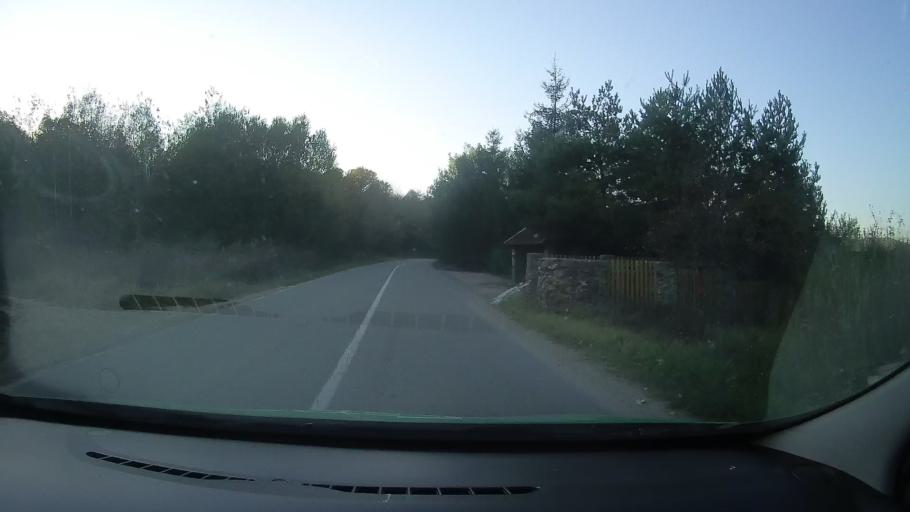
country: RO
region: Timis
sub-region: Comuna Fardea
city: Fardea
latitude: 45.7466
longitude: 22.1393
